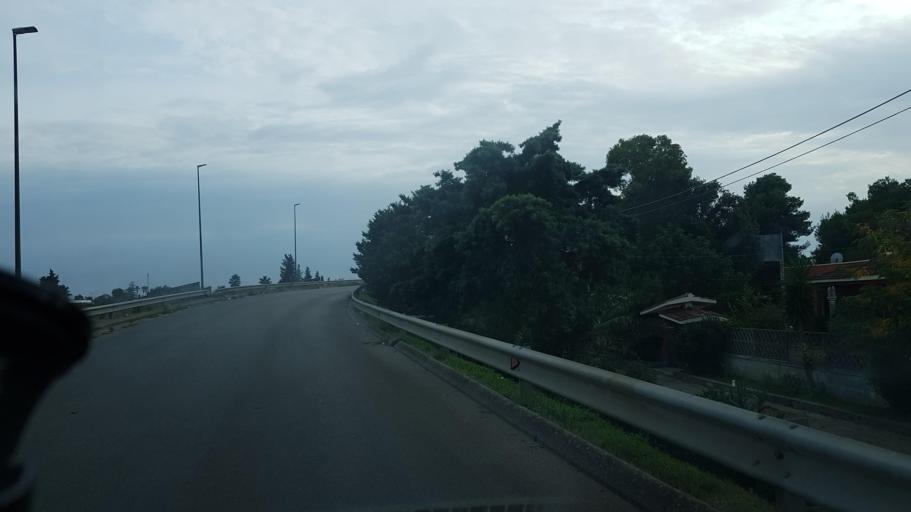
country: IT
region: Apulia
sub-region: Provincia di Lecce
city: Trepuzzi
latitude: 40.4143
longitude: 18.0739
